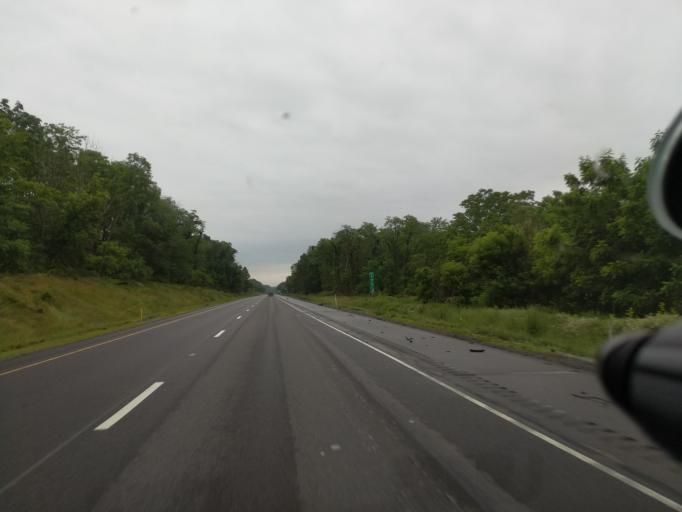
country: US
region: Pennsylvania
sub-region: Clinton County
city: Mill Hall
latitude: 41.0501
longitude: -77.4453
